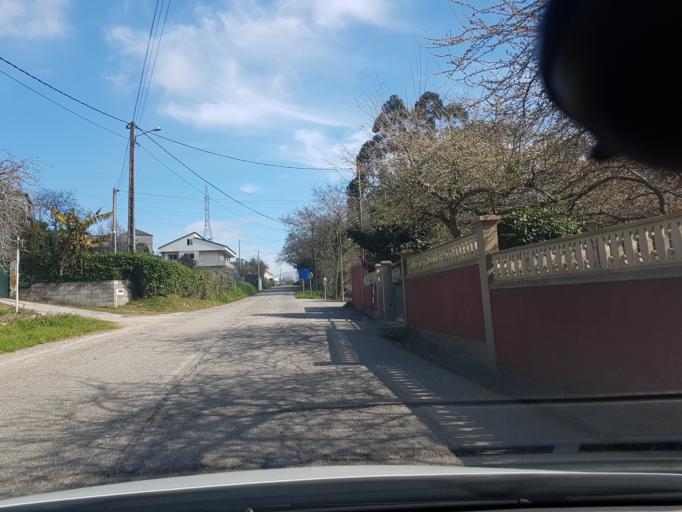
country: ES
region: Galicia
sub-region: Provincia de Pontevedra
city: Porrino
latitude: 42.2136
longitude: -8.6422
